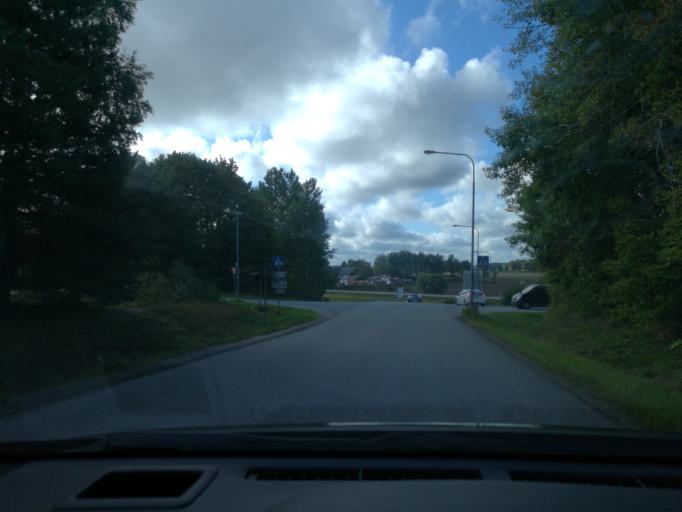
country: SE
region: Stockholm
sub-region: Vallentuna Kommun
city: Vallentuna
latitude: 59.5433
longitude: 18.0499
